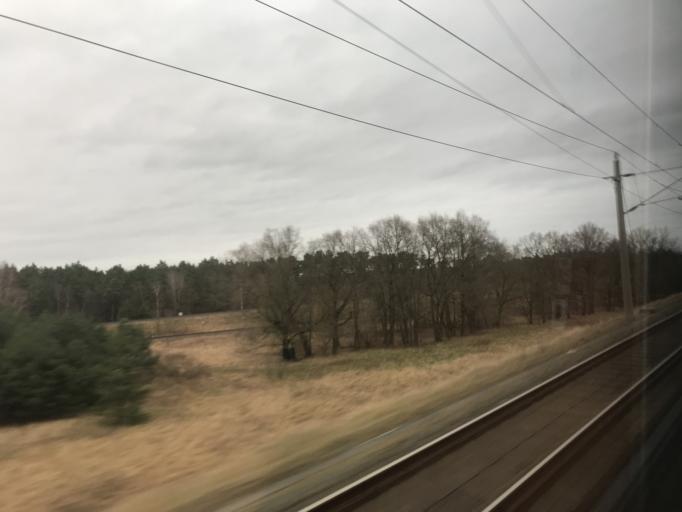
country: DE
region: Saxony-Anhalt
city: Hassel
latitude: 52.5947
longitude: 11.9374
